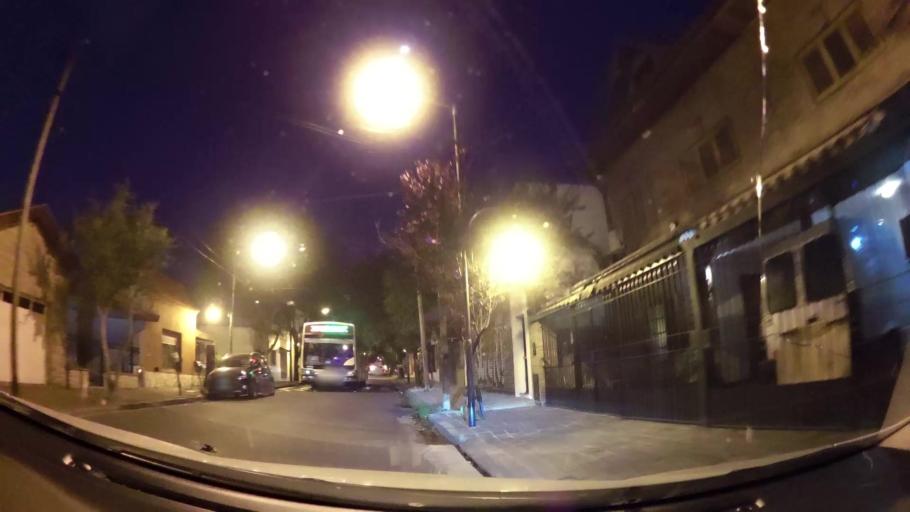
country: AR
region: Buenos Aires
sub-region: Partido de San Isidro
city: San Isidro
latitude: -34.4516
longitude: -58.5444
